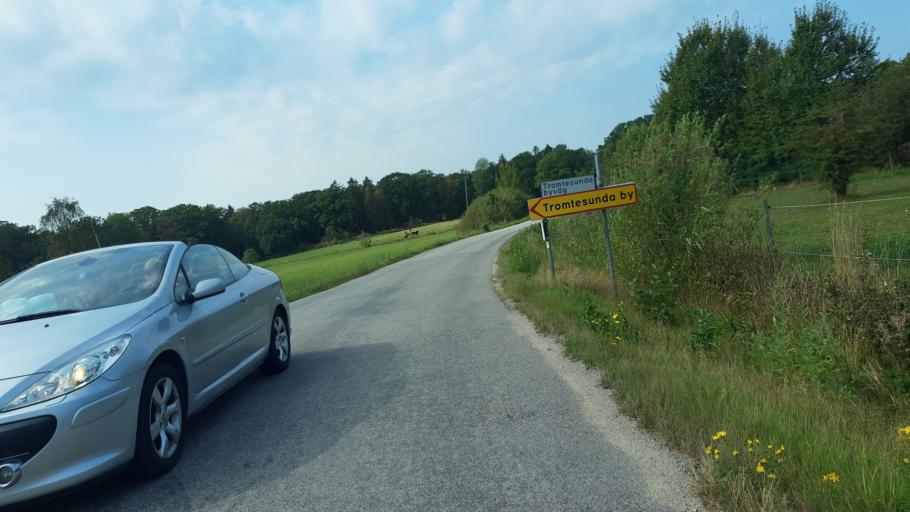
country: SE
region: Blekinge
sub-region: Karlskrona Kommun
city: Nattraby
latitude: 56.1757
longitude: 15.4800
